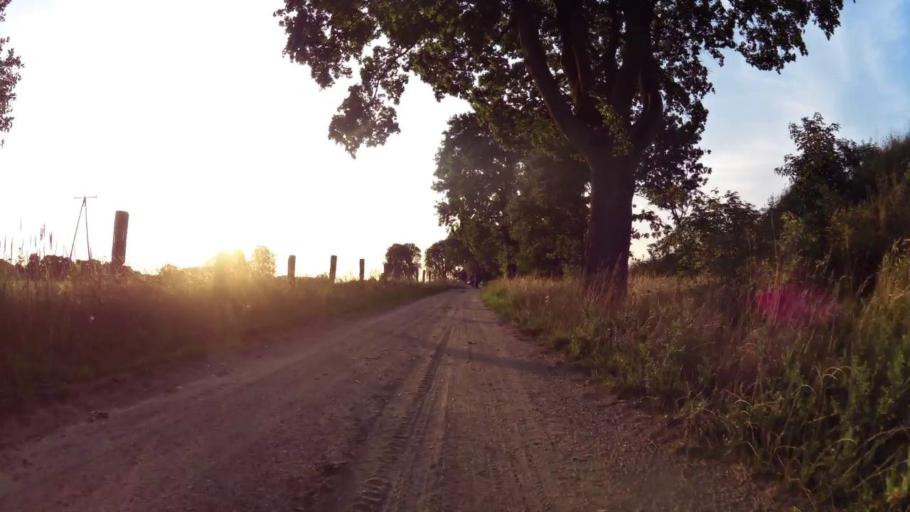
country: PL
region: West Pomeranian Voivodeship
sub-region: Powiat drawski
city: Drawsko Pomorskie
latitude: 53.4971
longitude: 15.7537
